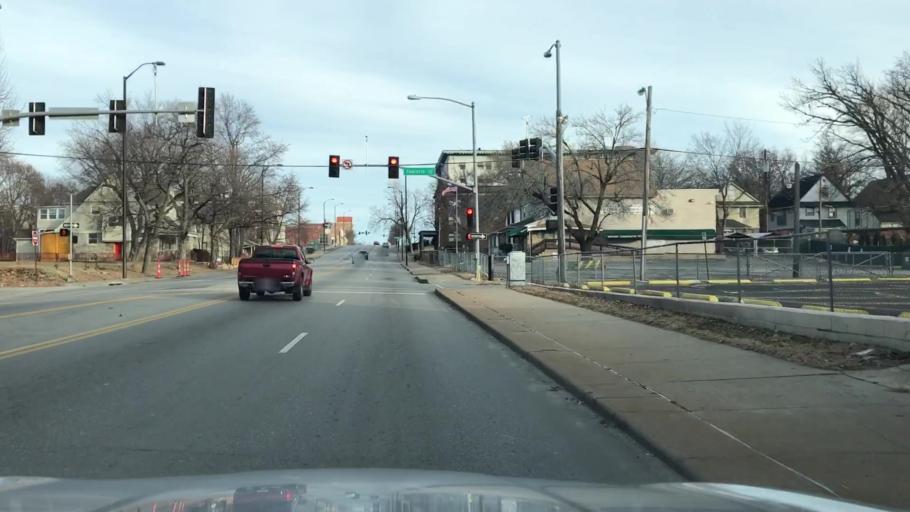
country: US
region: Missouri
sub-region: Jackson County
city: Kansas City
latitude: 39.0688
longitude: -94.5760
